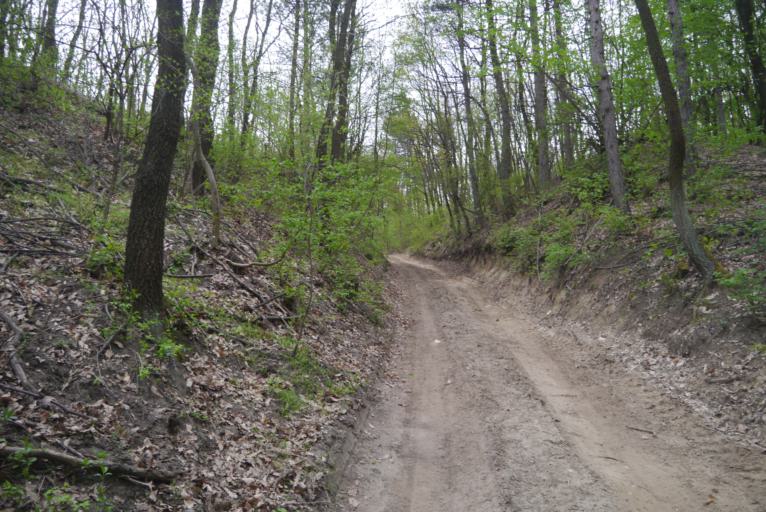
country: HU
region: Komarom-Esztergom
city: Piliscsev
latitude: 47.6628
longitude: 18.8299
